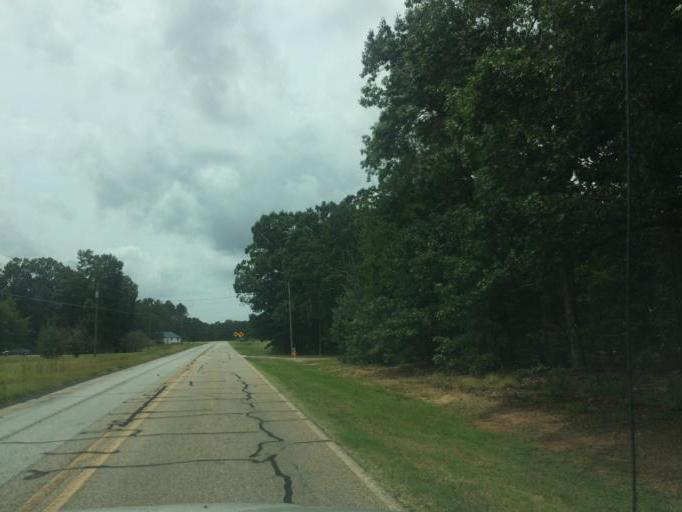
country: US
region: Georgia
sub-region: Hart County
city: Hartwell
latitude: 34.2859
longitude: -82.8620
